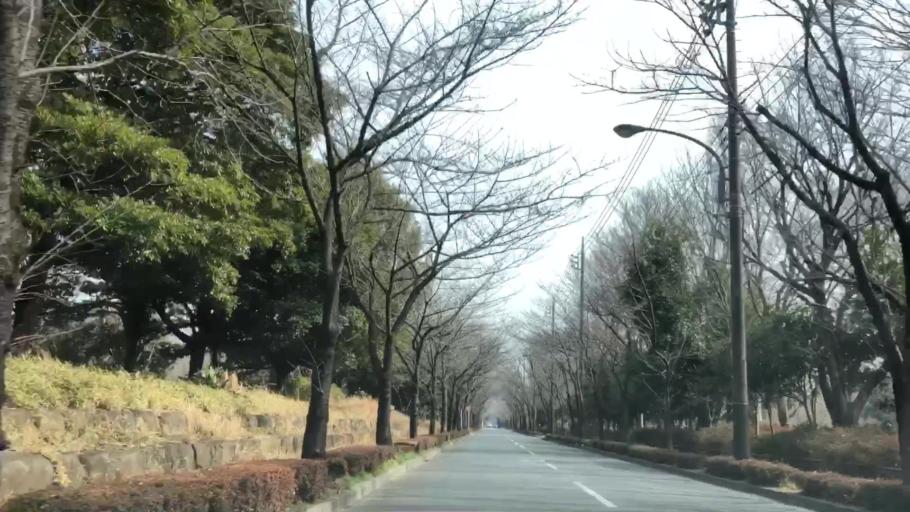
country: JP
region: Saitama
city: Wako
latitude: 35.7764
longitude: 139.5982
